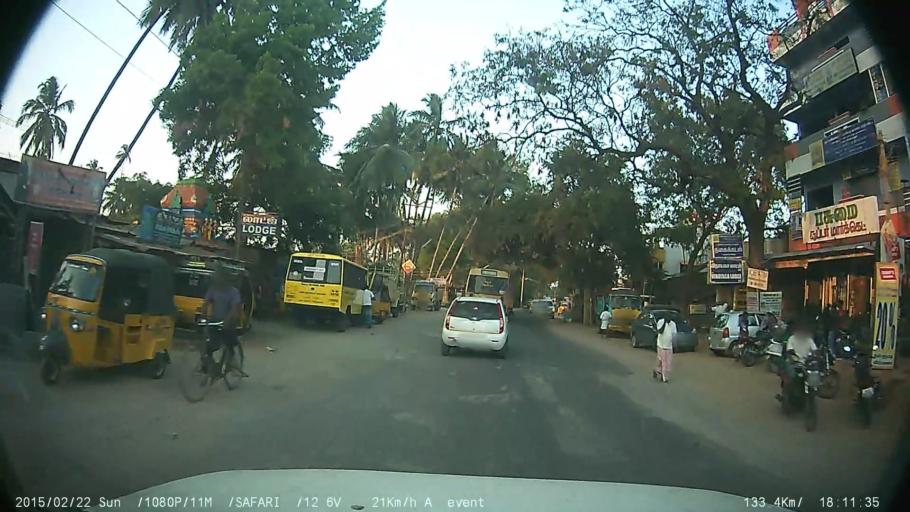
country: IN
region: Tamil Nadu
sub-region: Theni
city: Chinnamanur
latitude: 9.8443
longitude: 77.3805
